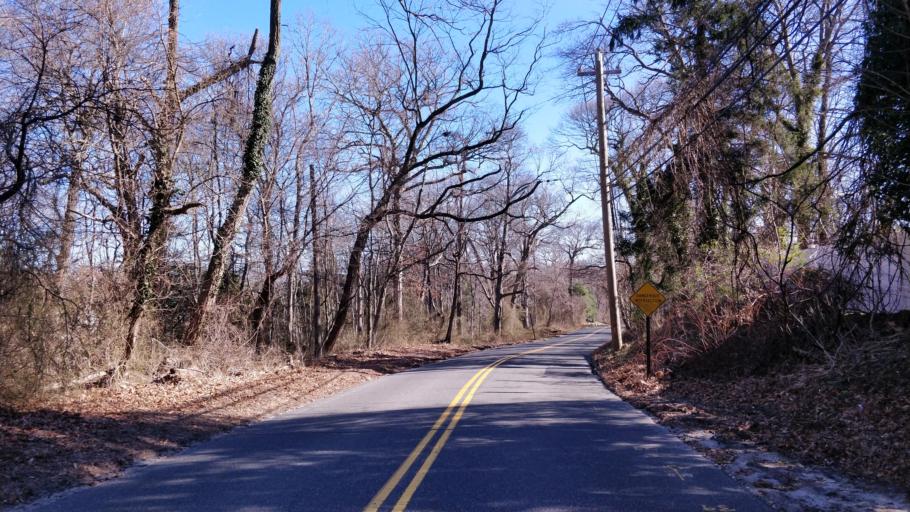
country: US
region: New York
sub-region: Suffolk County
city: Port Jefferson
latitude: 40.9484
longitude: -73.0497
